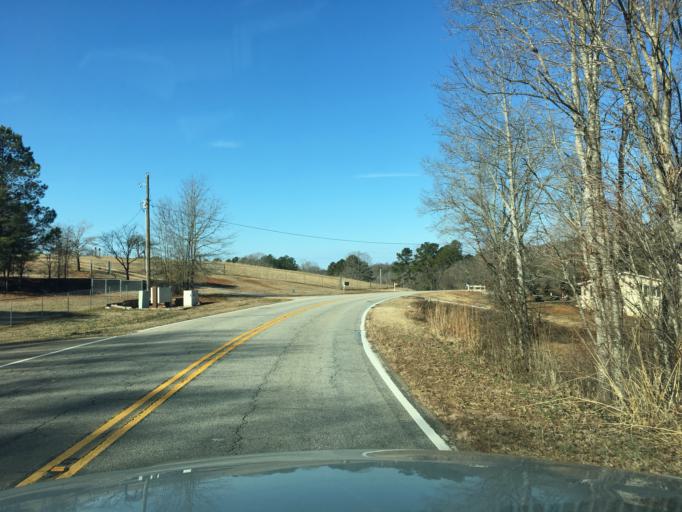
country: US
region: South Carolina
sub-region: Pickens County
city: Pickens
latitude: 34.8753
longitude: -82.6713
